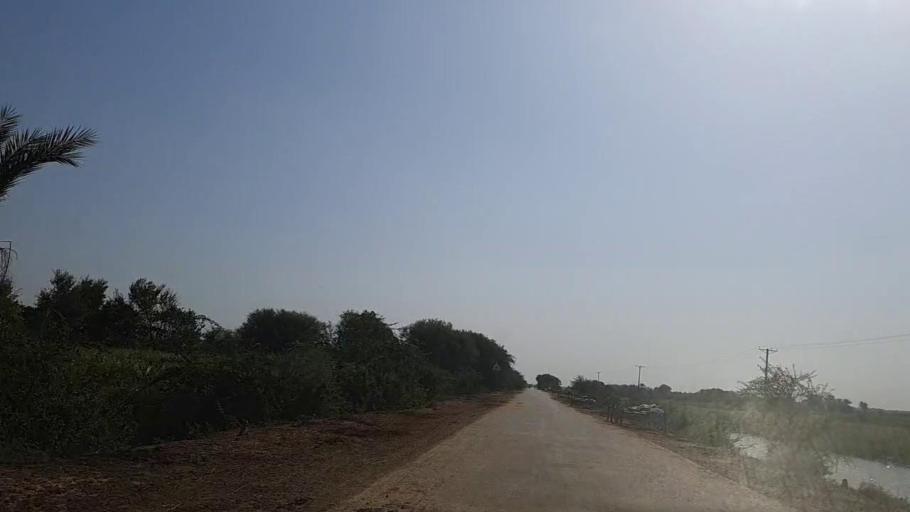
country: PK
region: Sindh
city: Mirpur Batoro
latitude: 24.5960
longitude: 68.2933
